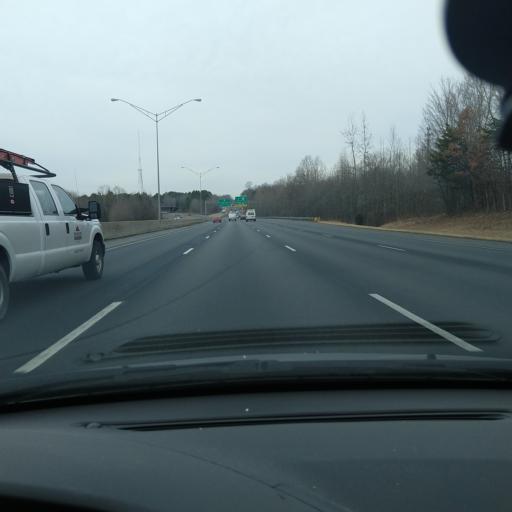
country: US
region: North Carolina
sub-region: Forsyth County
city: Kernersville
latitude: 36.0964
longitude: -80.0096
